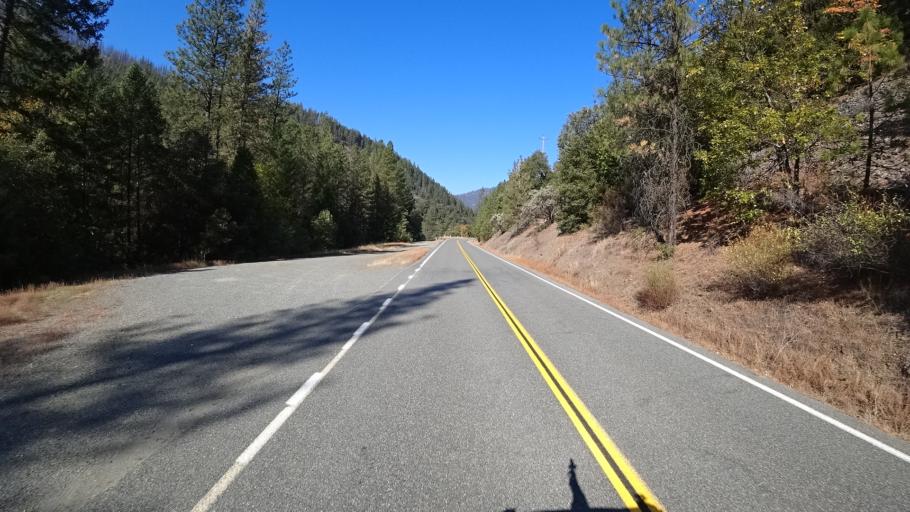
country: US
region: California
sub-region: Siskiyou County
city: Happy Camp
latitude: 41.7671
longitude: -123.0227
